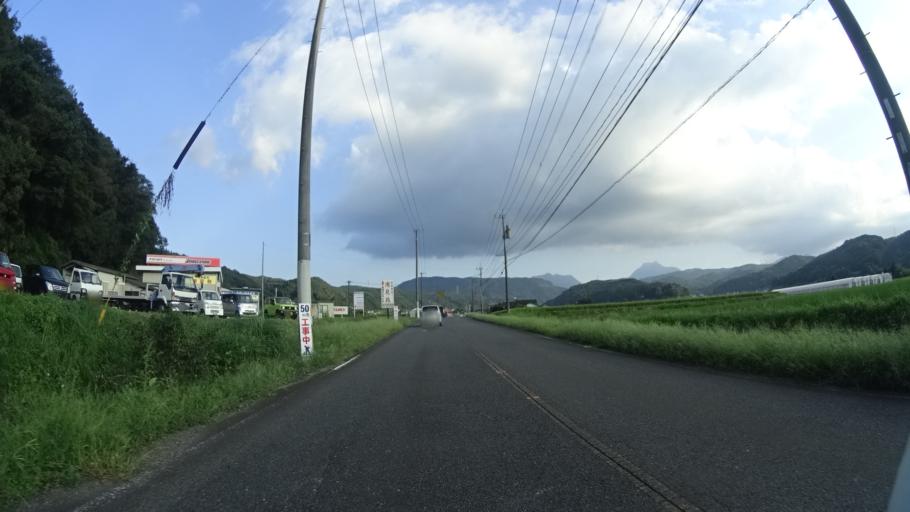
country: JP
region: Oita
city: Hiji
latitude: 33.3993
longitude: 131.3898
